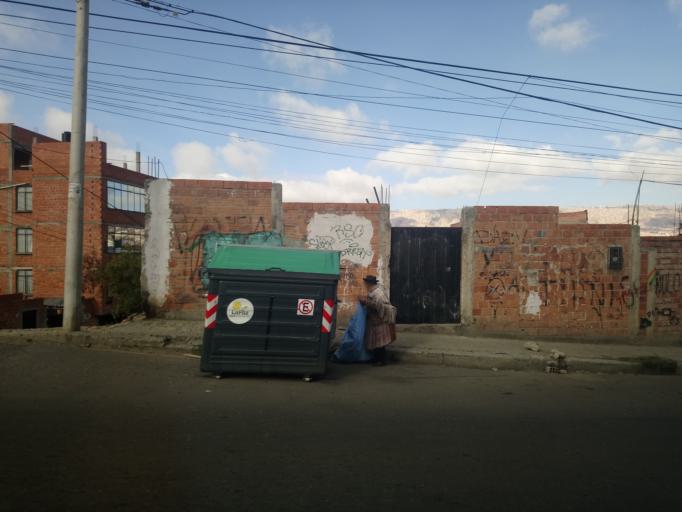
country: BO
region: La Paz
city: La Paz
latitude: -16.4960
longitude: -68.1121
